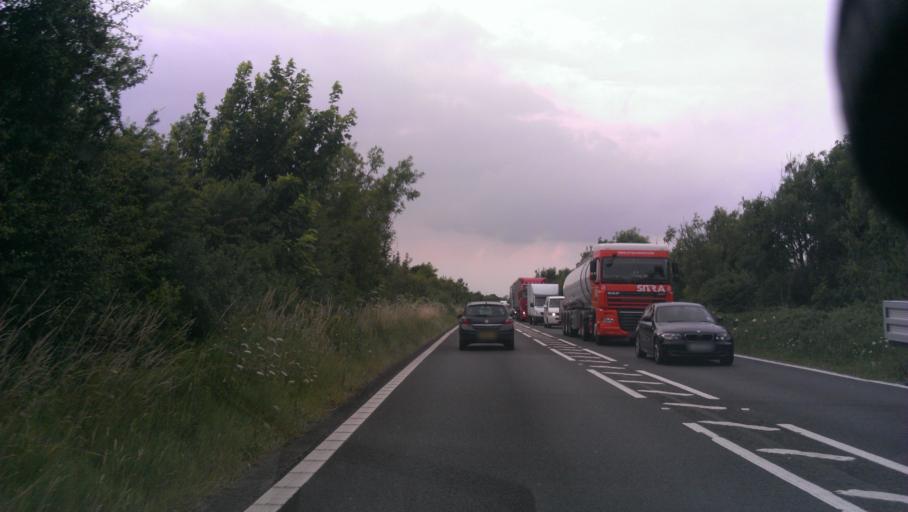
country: GB
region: England
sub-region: Kent
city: Shepherdswell
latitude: 51.1624
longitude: 1.2656
